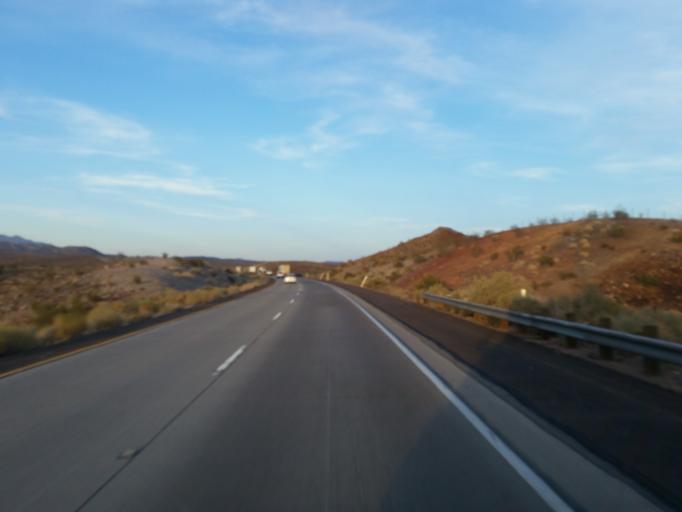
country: US
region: California
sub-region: San Bernardino County
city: Twentynine Palms
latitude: 34.7204
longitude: -115.9898
